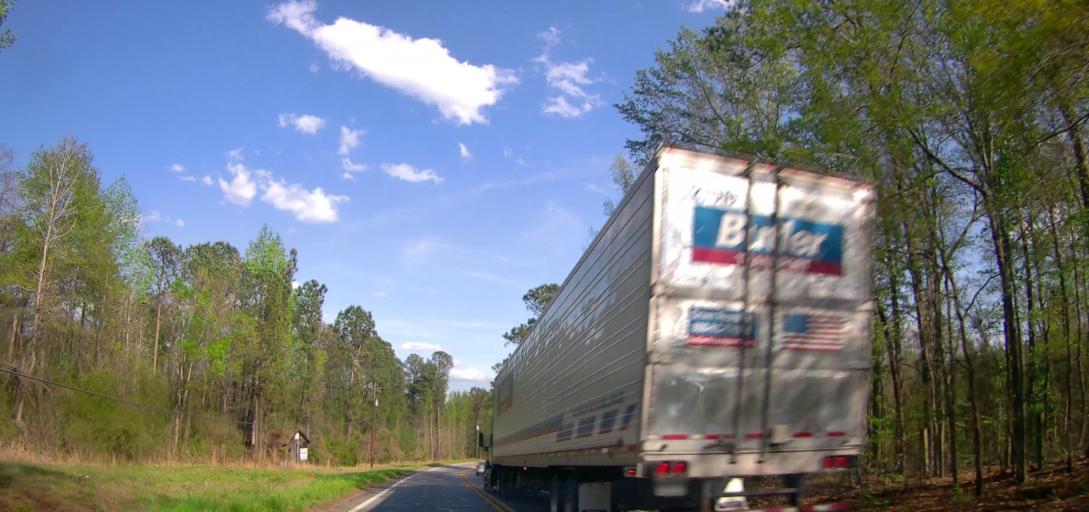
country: US
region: Georgia
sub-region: Baldwin County
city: Hardwick
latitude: 33.0909
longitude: -83.1787
